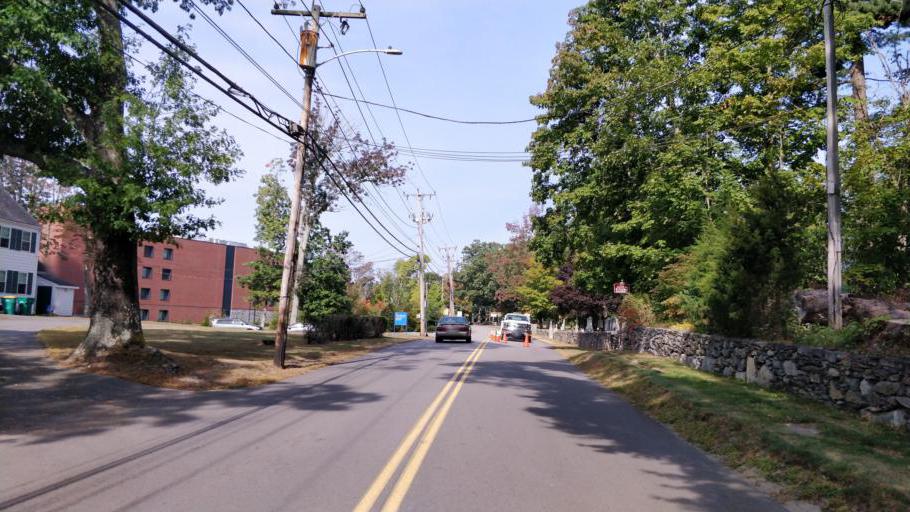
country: US
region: Massachusetts
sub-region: Bristol County
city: Norton Center
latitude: 41.9680
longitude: -71.1797
